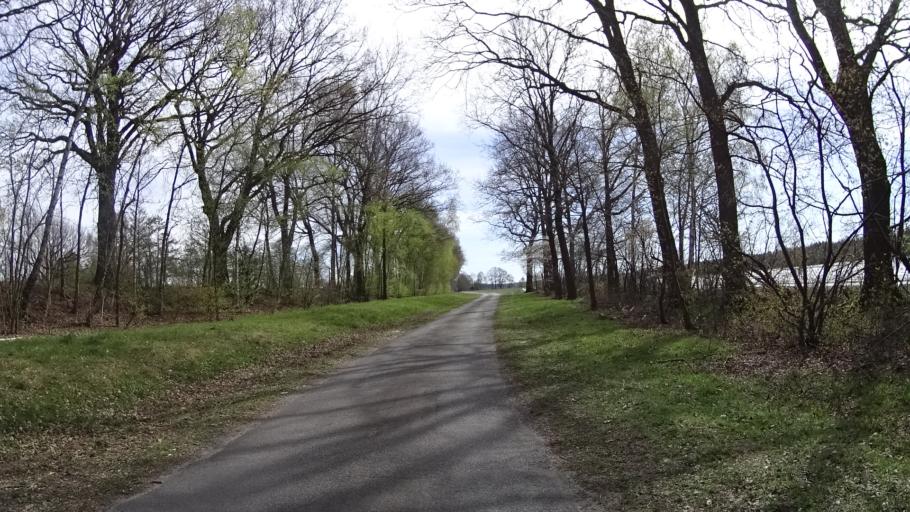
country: DE
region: Lower Saxony
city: Lunne
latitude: 52.4021
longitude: 7.3783
